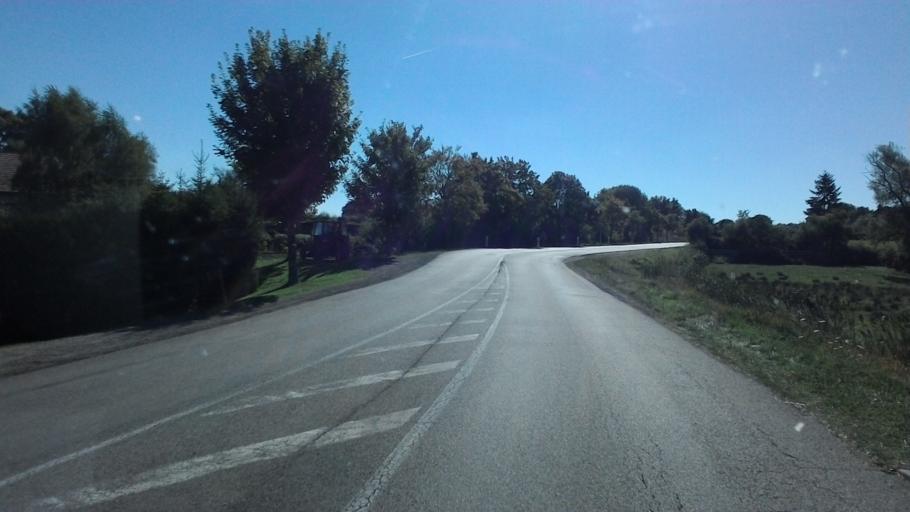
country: FR
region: Bourgogne
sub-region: Departement de la Cote-d'Or
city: Saulieu
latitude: 47.2770
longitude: 4.2382
